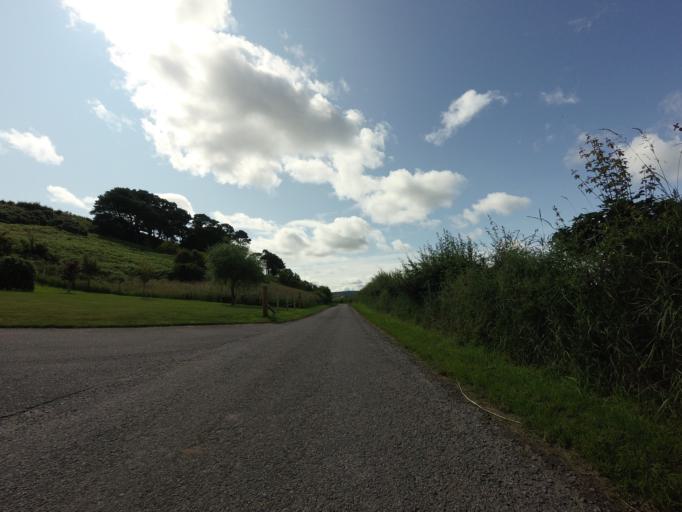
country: GB
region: Scotland
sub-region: Moray
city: Kinloss
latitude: 57.6400
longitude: -3.5214
